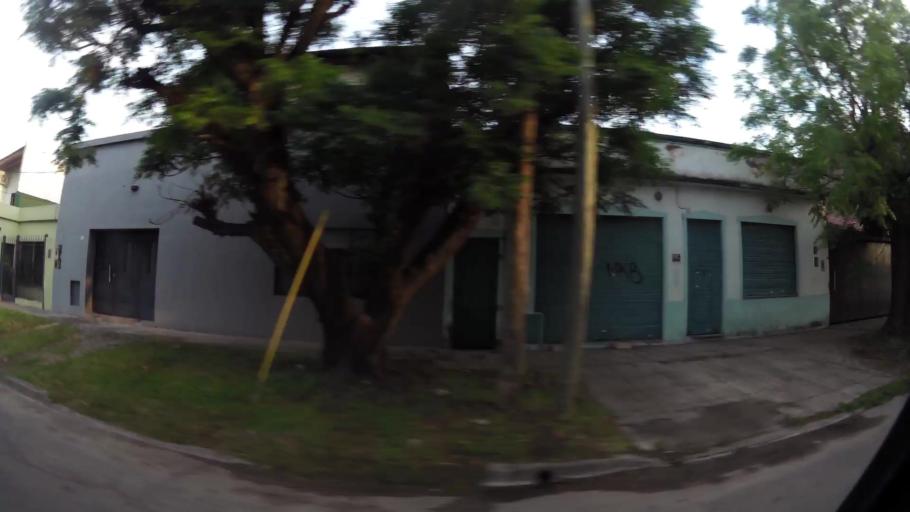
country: AR
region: Buenos Aires
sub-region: Partido de Almirante Brown
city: Adrogue
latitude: -34.7588
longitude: -58.3465
